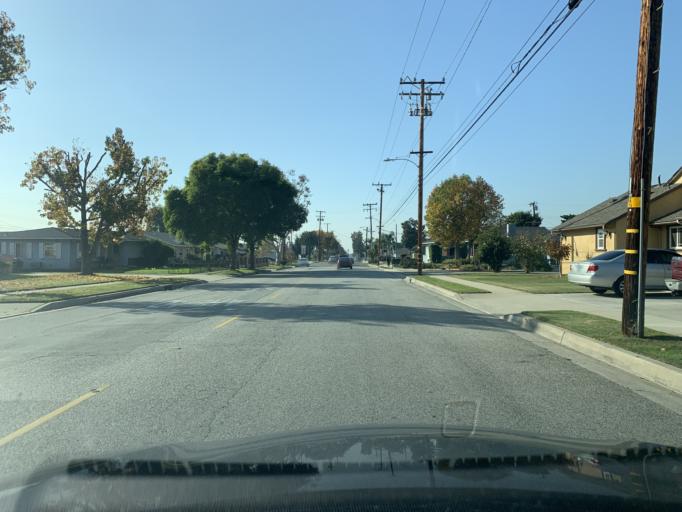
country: US
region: California
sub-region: Los Angeles County
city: Covina
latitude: 34.0754
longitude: -117.8974
